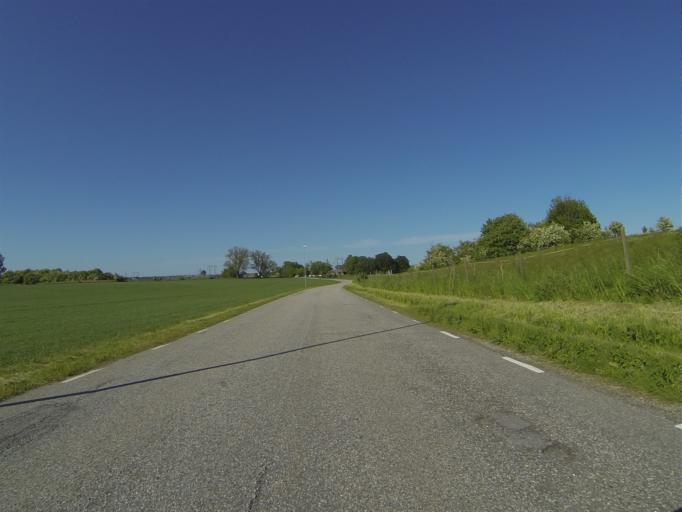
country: SE
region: Skane
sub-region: Malmo
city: Oxie
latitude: 55.5947
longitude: 13.1305
